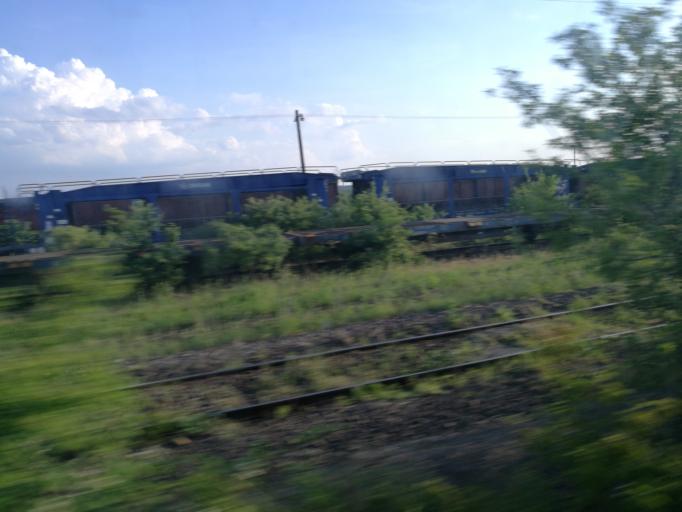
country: RO
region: Arges
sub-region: Comuna Calinesti
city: Vranesti
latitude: 44.8317
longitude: 24.9883
